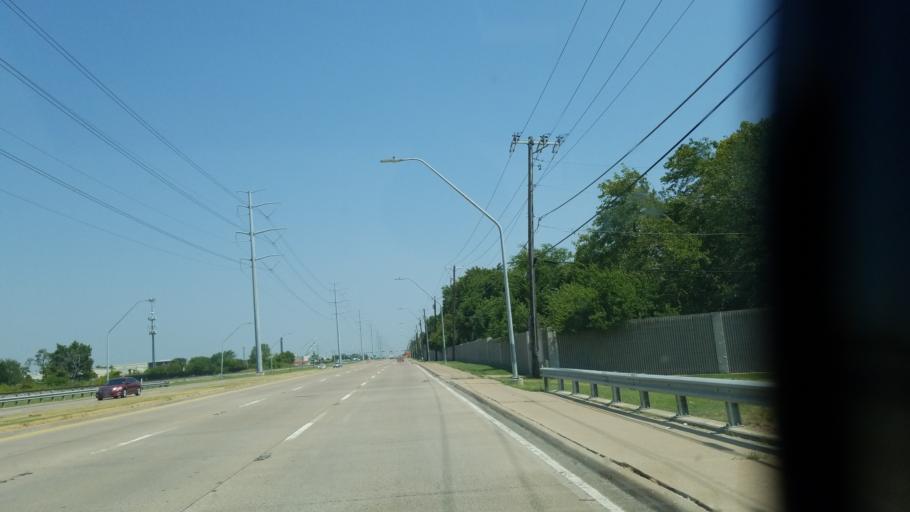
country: US
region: Texas
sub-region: Dallas County
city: Garland
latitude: 32.9261
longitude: -96.6269
